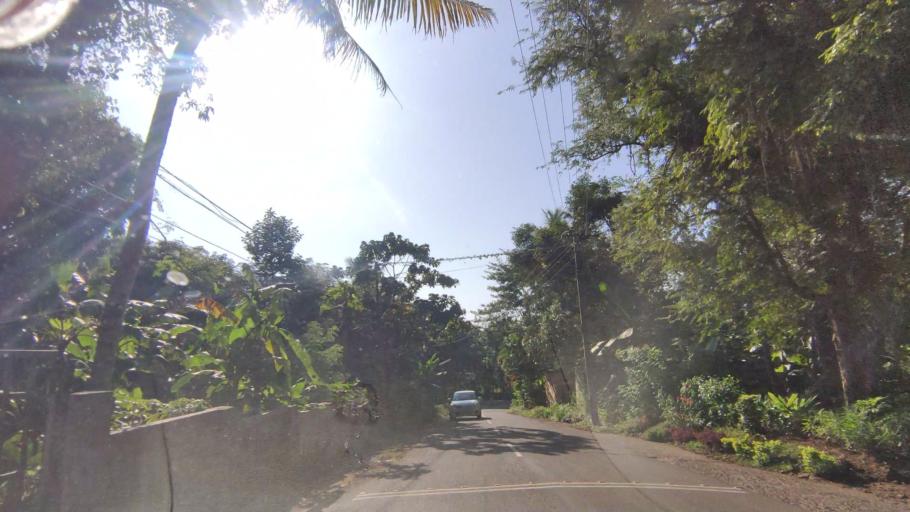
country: IN
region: Kerala
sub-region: Kottayam
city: Kottayam
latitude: 9.5581
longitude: 76.5091
